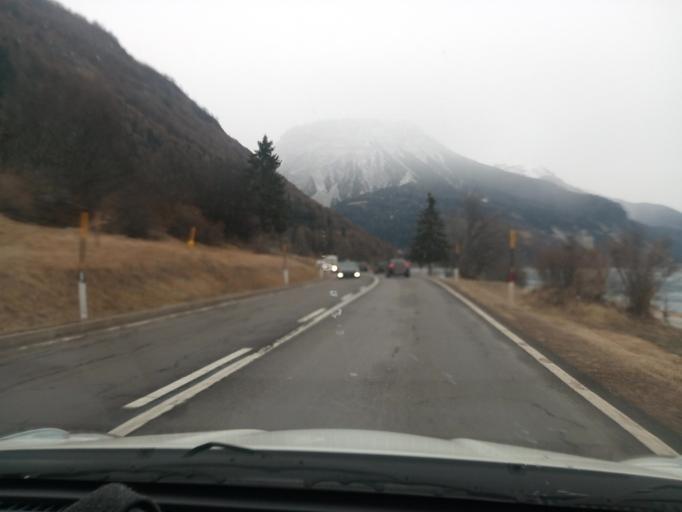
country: IT
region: Trentino-Alto Adige
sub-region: Bolzano
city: Curon Venosta
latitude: 46.8199
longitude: 10.5242
